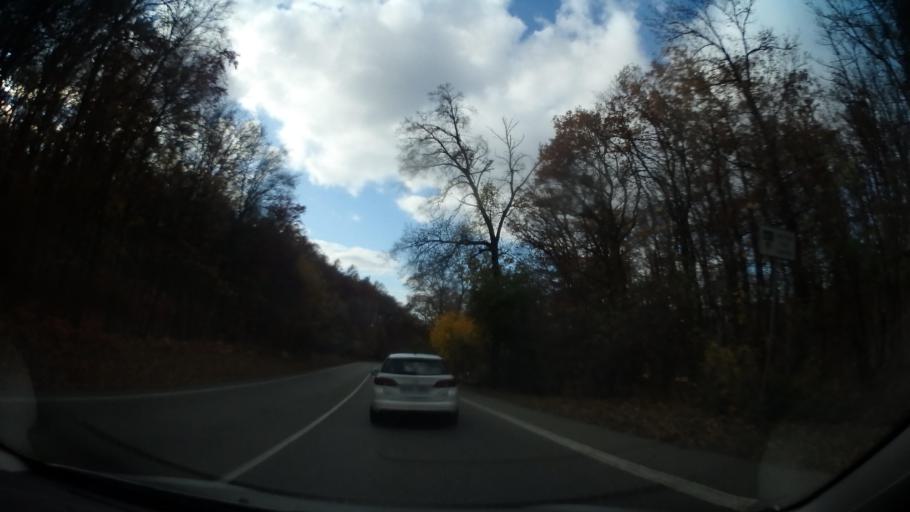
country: CZ
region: South Moravian
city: Troubsko
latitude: 49.1969
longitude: 16.5291
